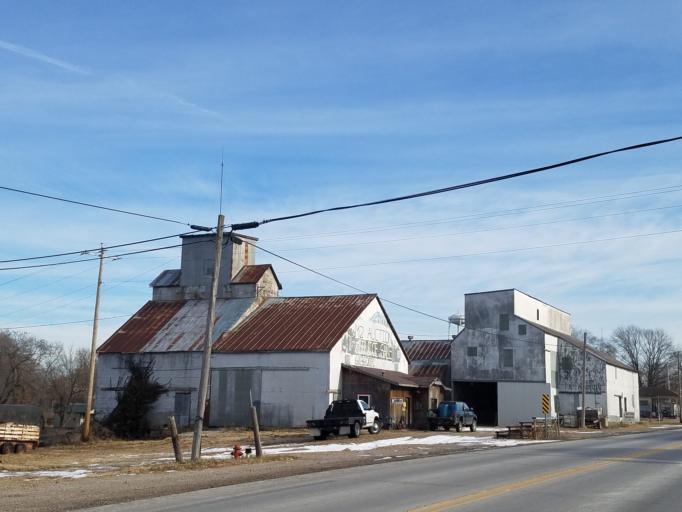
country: US
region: Missouri
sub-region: Moniteau County
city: Tipton
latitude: 38.6697
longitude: -92.8737
